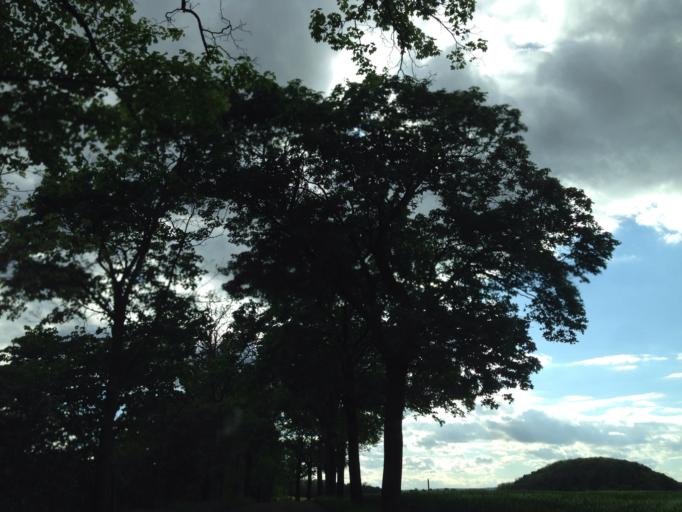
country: DE
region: Thuringia
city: Bodelwitz
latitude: 50.6845
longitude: 11.6121
